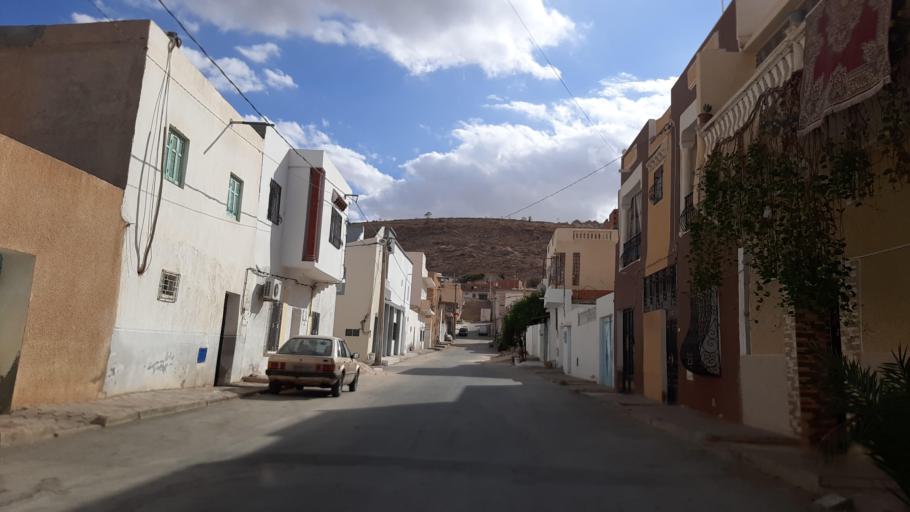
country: TN
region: Tataouine
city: Tataouine
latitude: 32.9270
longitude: 10.4530
